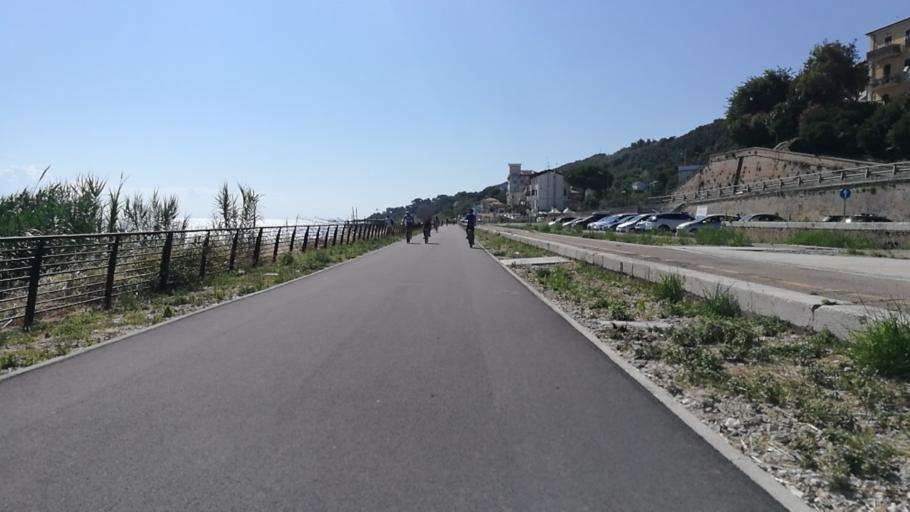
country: IT
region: Abruzzo
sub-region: Provincia di Chieti
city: Marina di San Vito
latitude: 42.3075
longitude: 14.4482
